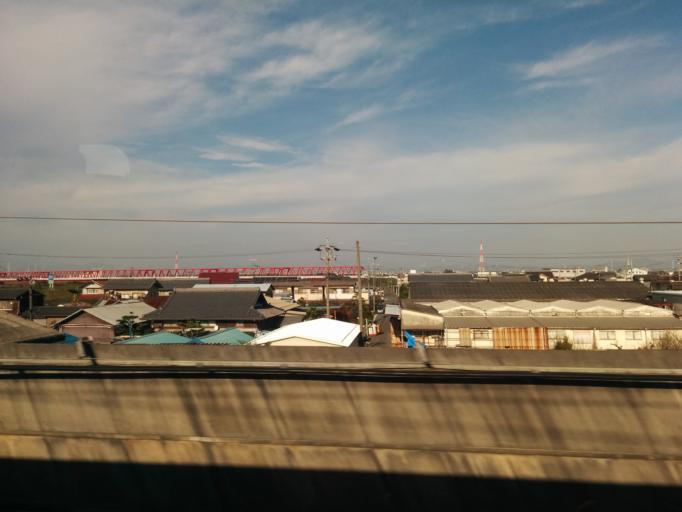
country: JP
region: Gifu
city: Ogaki
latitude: 35.3392
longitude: 136.6538
